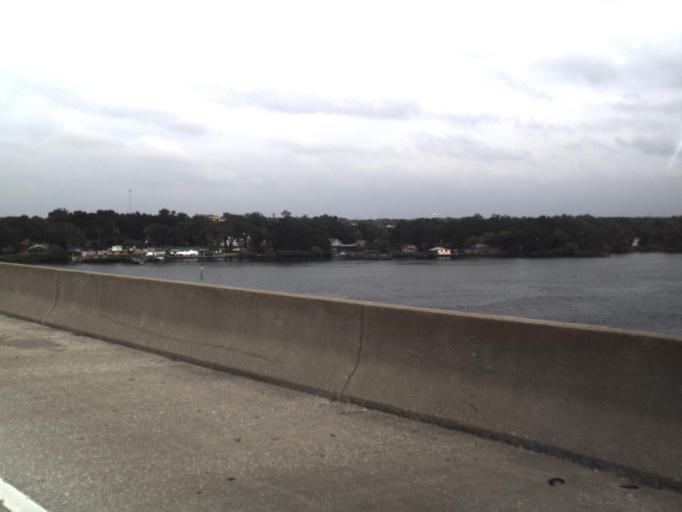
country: US
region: Florida
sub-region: Manatee County
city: Ellenton
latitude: 27.5248
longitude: -82.5059
